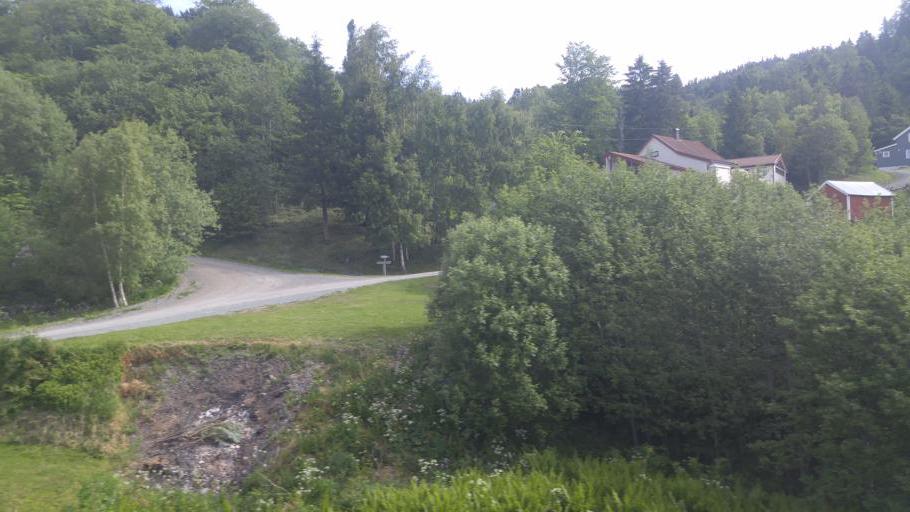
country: NO
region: Sor-Trondelag
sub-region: Melhus
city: Melhus
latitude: 63.2207
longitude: 10.3025
